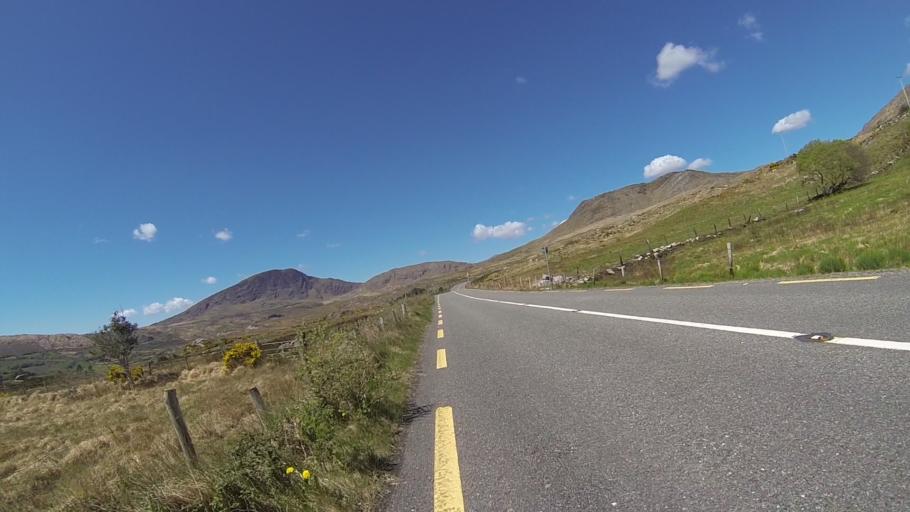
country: IE
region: Munster
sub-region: Ciarrai
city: Kenmare
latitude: 51.9209
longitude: -9.6274
